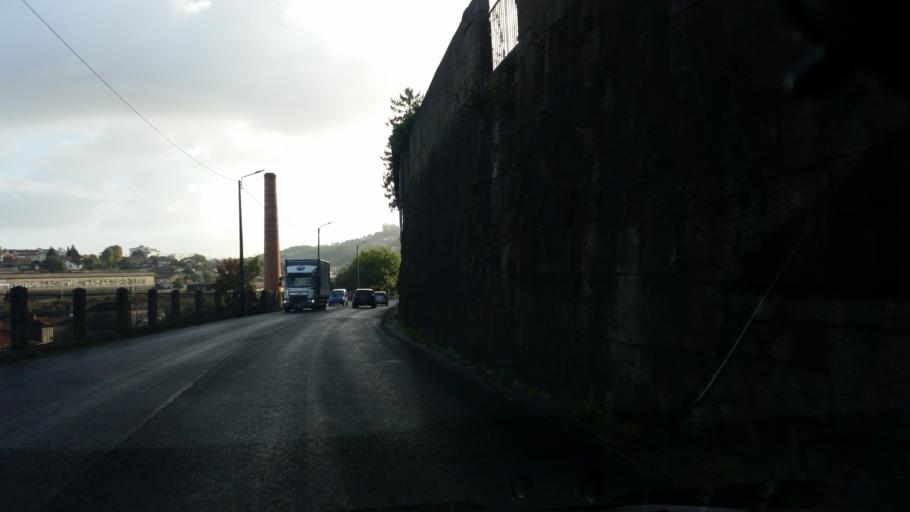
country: PT
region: Porto
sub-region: Santo Tirso
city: Aves
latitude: 41.3563
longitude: -8.4164
